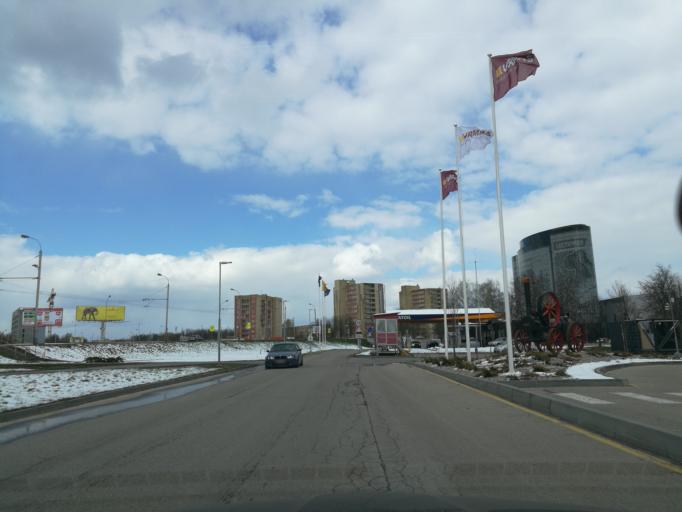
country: LT
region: Kauno apskritis
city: Dainava (Kaunas)
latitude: 54.9152
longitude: 23.9862
